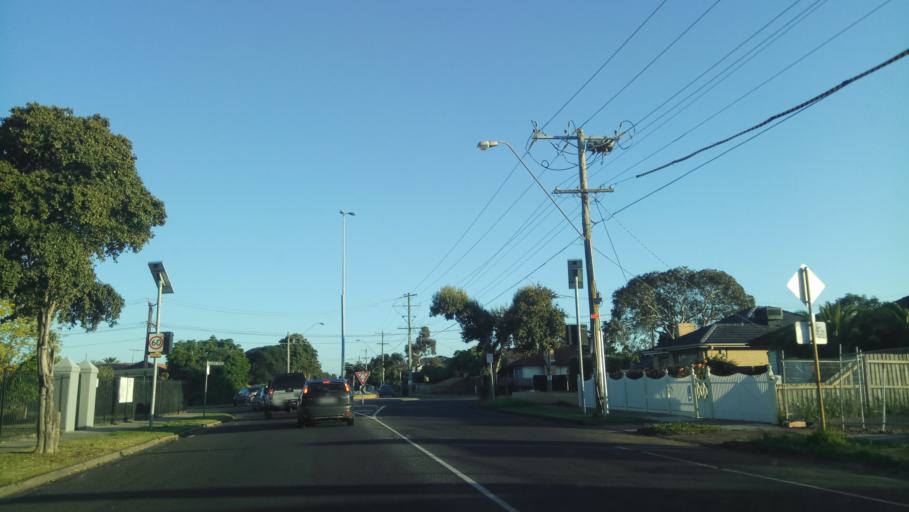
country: AU
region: Victoria
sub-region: Hobsons Bay
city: Altona
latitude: -37.8637
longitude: 144.8122
